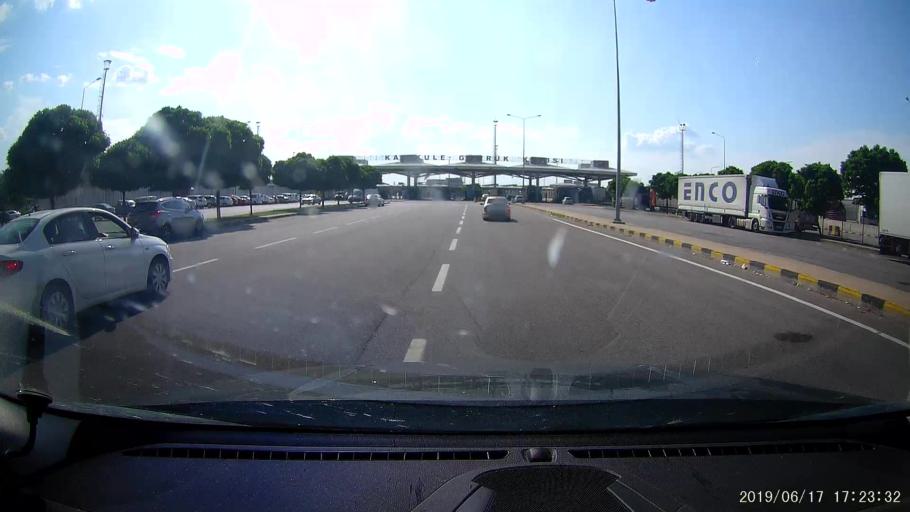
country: GR
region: East Macedonia and Thrace
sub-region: Nomos Evrou
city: Rizia
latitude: 41.7144
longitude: 26.3643
